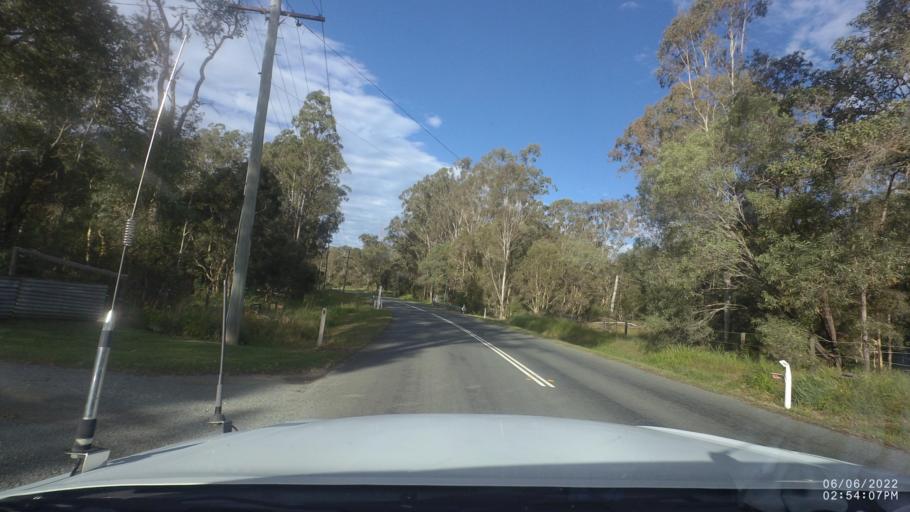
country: AU
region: Queensland
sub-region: Logan
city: Cedar Vale
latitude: -27.8552
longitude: 153.0461
